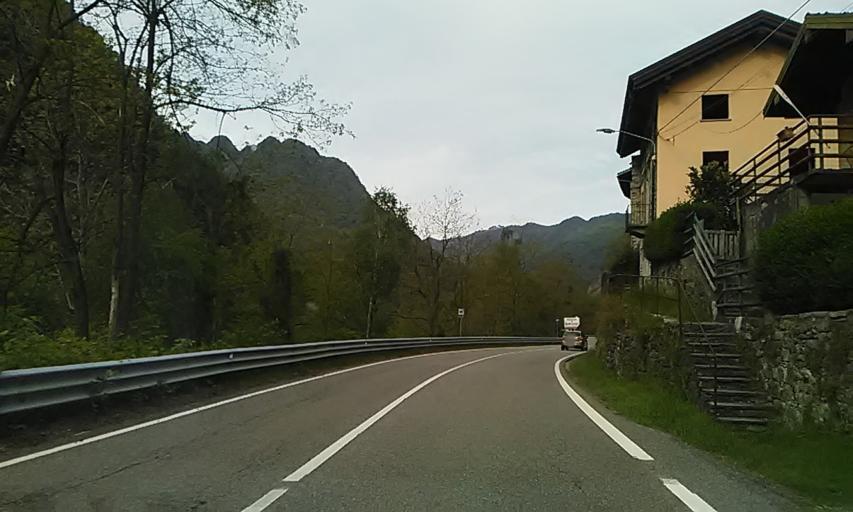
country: IT
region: Piedmont
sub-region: Provincia di Vercelli
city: Vocca
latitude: 45.8288
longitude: 8.1810
